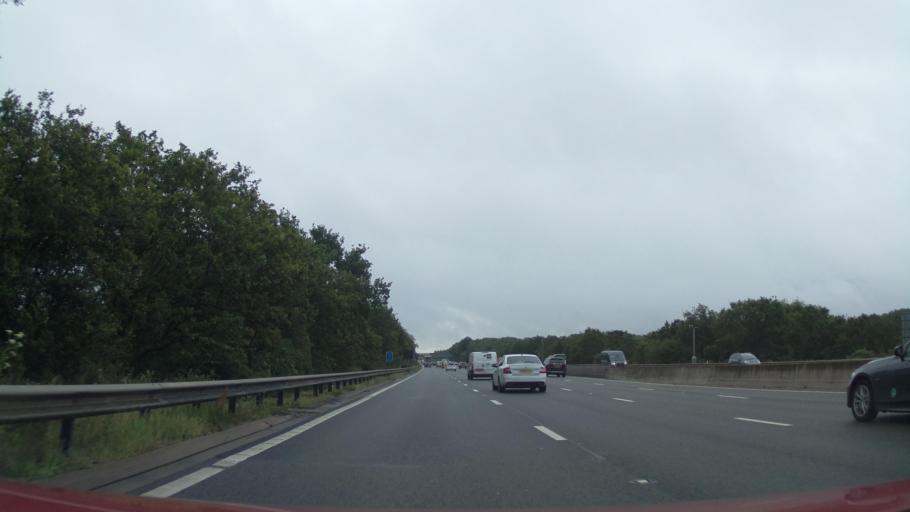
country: GB
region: England
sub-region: Surrey
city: Windlesham
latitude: 51.3683
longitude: -0.6306
